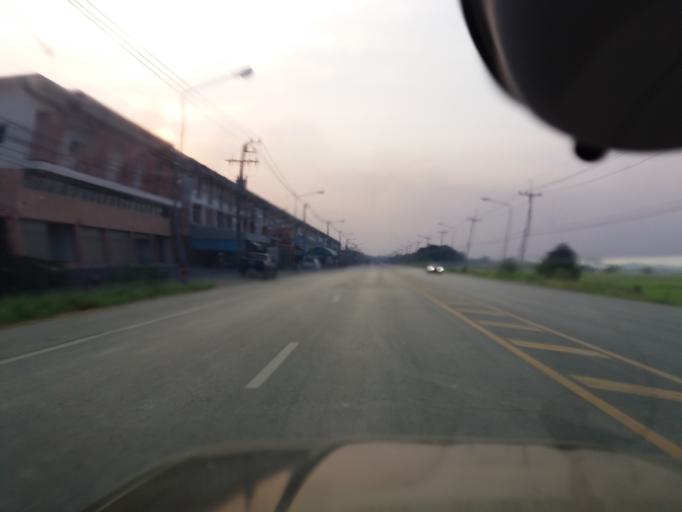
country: TH
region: Sing Buri
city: Bang Racham
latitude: 14.8827
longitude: 100.3356
